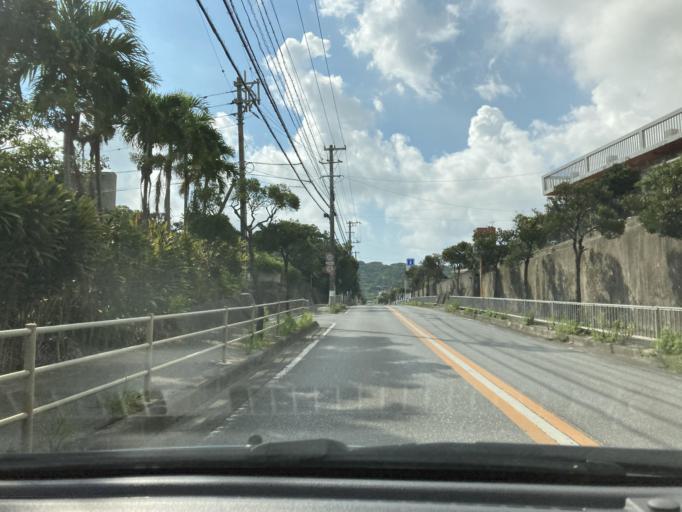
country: JP
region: Okinawa
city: Tomigusuku
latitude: 26.1547
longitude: 127.7502
